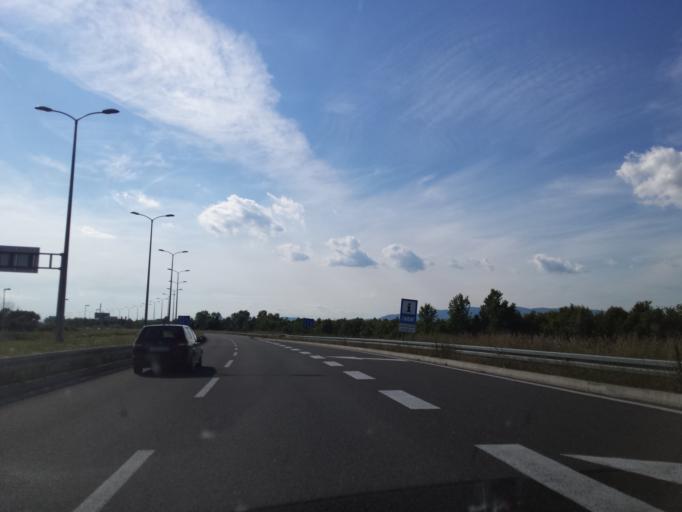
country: HR
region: Zagrebacka
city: Micevec
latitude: 45.7663
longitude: 16.0865
